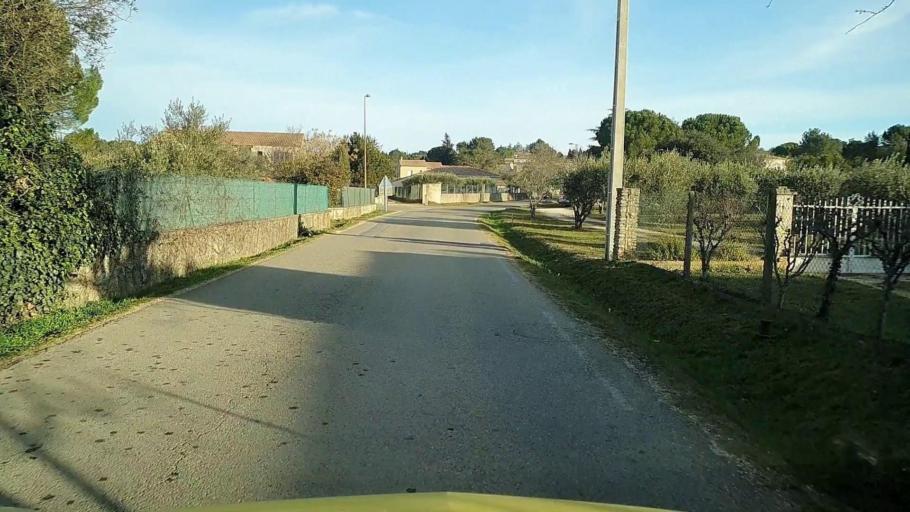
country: FR
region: Languedoc-Roussillon
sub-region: Departement du Gard
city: Castillon-du-Gard
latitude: 43.9577
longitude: 4.5514
